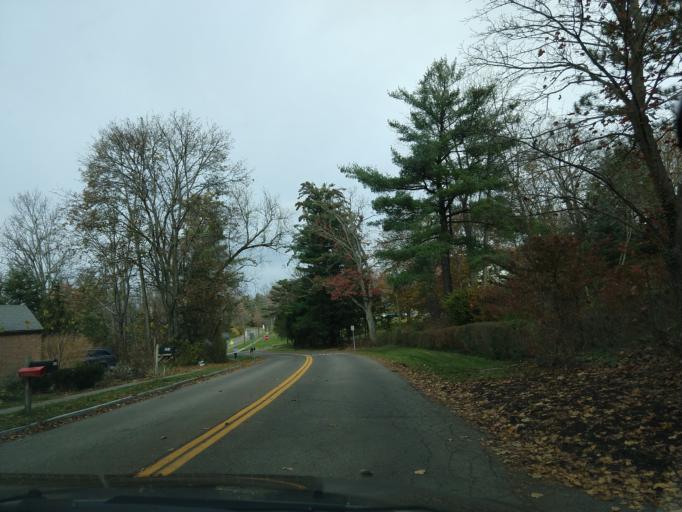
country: US
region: New York
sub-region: Tompkins County
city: Cayuga Heights
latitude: 42.4642
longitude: -76.4900
